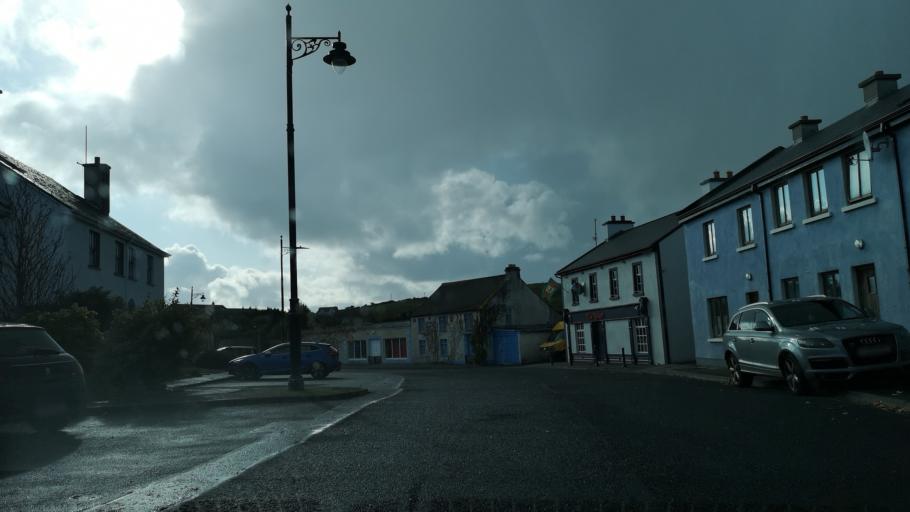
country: IE
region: Connaught
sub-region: Maigh Eo
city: Westport
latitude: 53.7987
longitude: -9.5516
